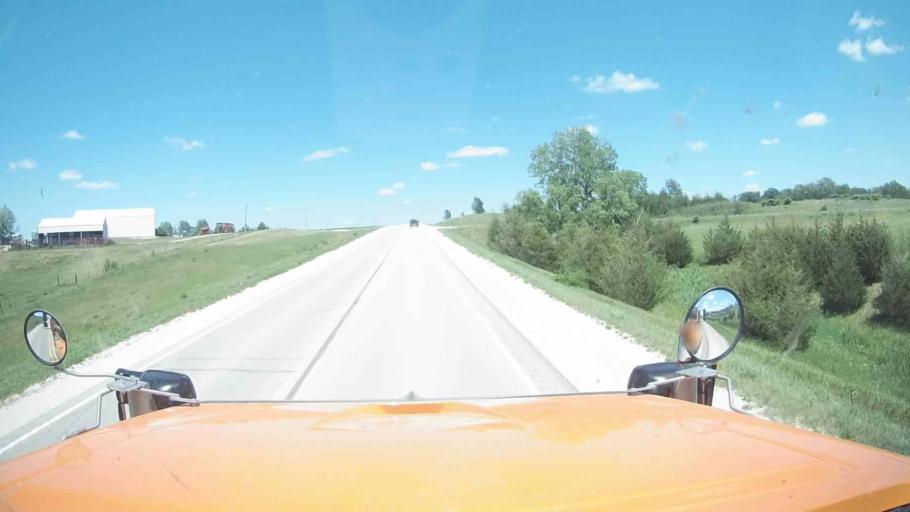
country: US
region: Iowa
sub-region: Adair County
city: Greenfield
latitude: 41.2746
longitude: -94.6104
